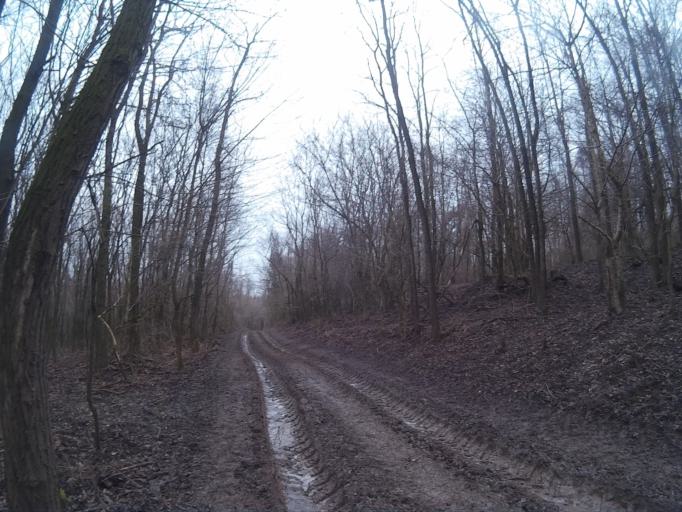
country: HU
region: Komarom-Esztergom
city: Tarjan
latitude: 47.5647
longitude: 18.5502
